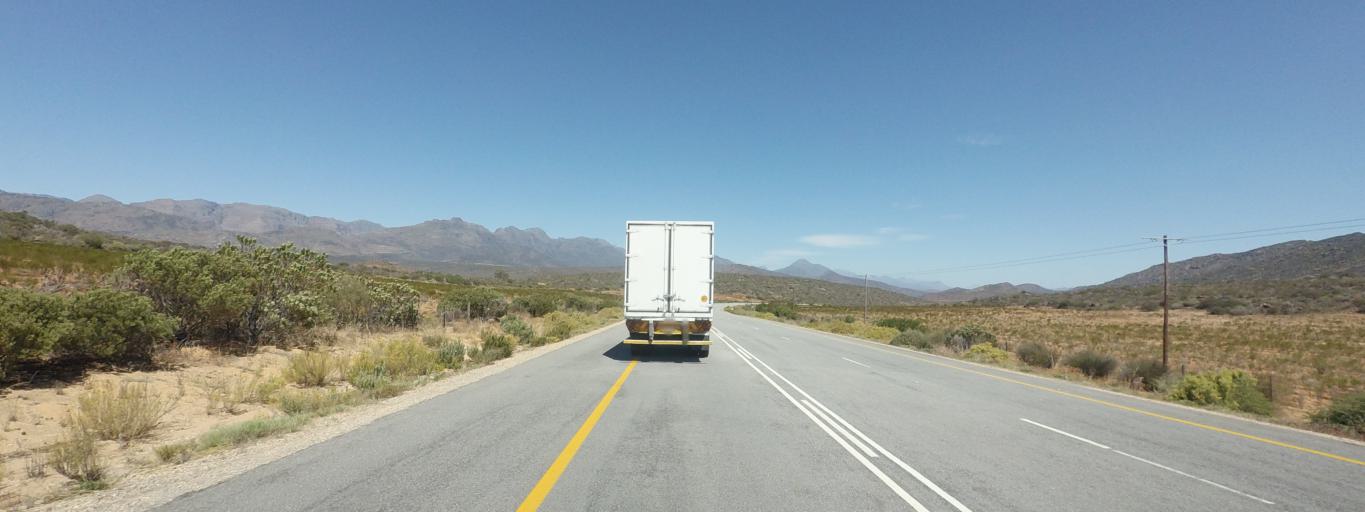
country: ZA
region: Western Cape
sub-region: West Coast District Municipality
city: Clanwilliam
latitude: -32.3255
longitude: 18.9204
